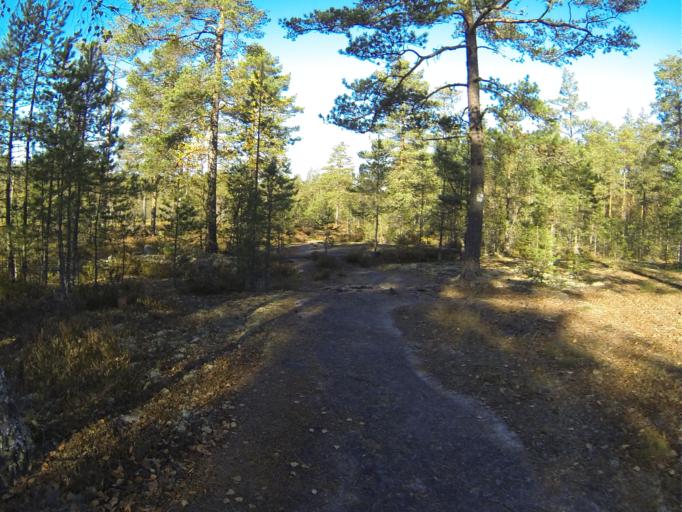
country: FI
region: Varsinais-Suomi
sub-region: Salo
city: Saerkisalo
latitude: 60.2025
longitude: 22.9234
